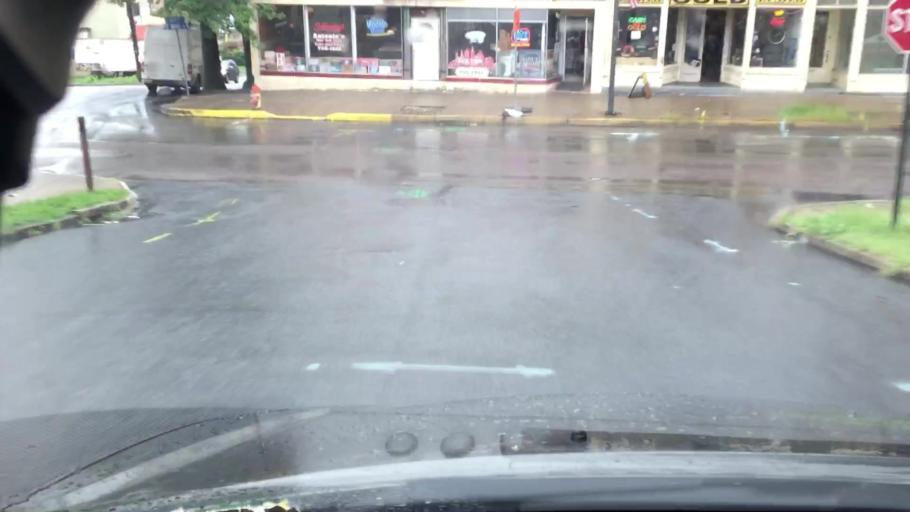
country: US
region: Pennsylvania
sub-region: Luzerne County
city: Nanticoke
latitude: 41.2054
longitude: -76.0015
